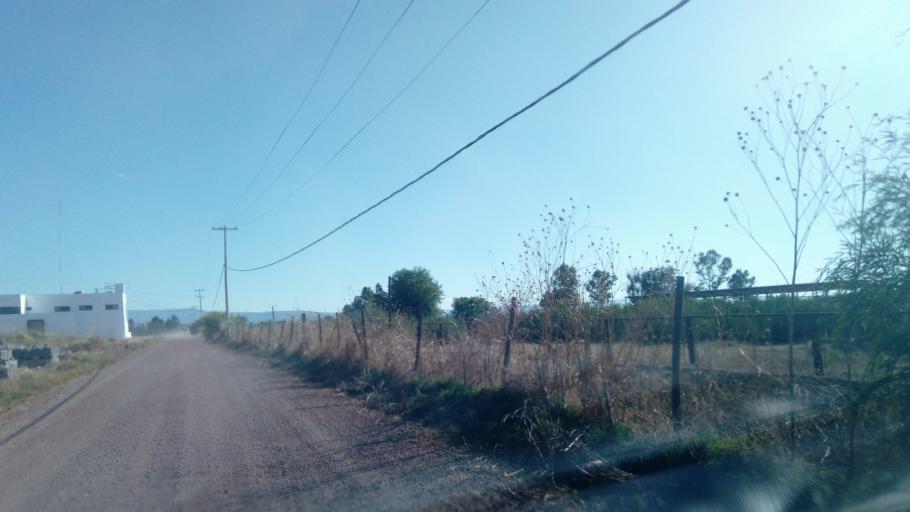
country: MX
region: Durango
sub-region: Durango
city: Jose Refugio Salcido
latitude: 24.0175
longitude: -104.5533
